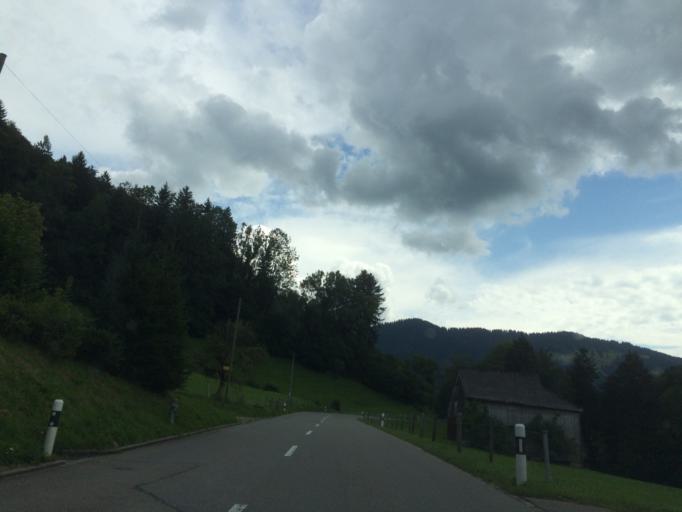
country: CH
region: Saint Gallen
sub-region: Wahlkreis Toggenburg
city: Krummenau
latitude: 47.2141
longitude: 9.2163
